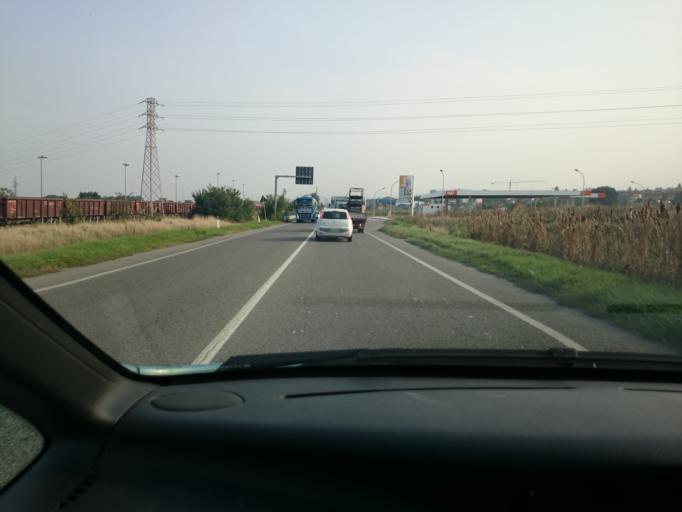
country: IT
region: Emilia-Romagna
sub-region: Provincia di Reggio Emilia
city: Casalgrande
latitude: 44.5789
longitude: 10.7433
